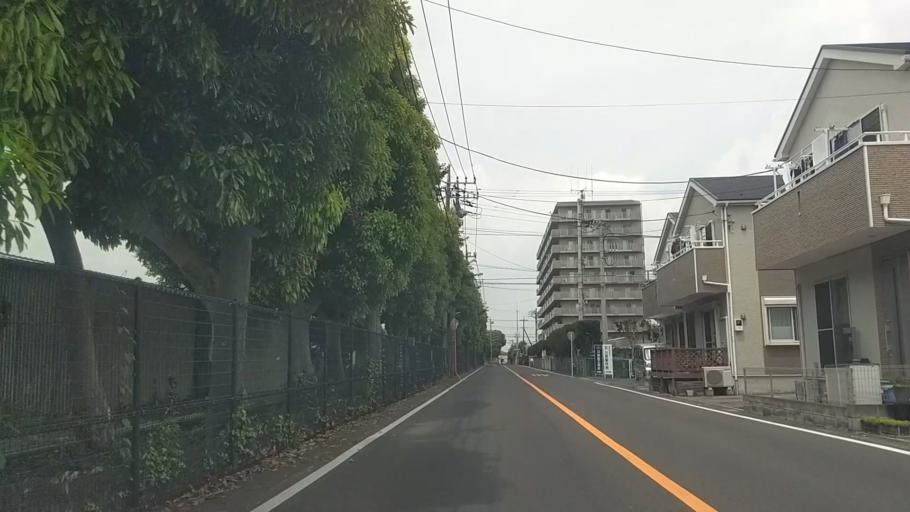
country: JP
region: Kanagawa
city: Fujisawa
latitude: 35.3606
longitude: 139.4641
